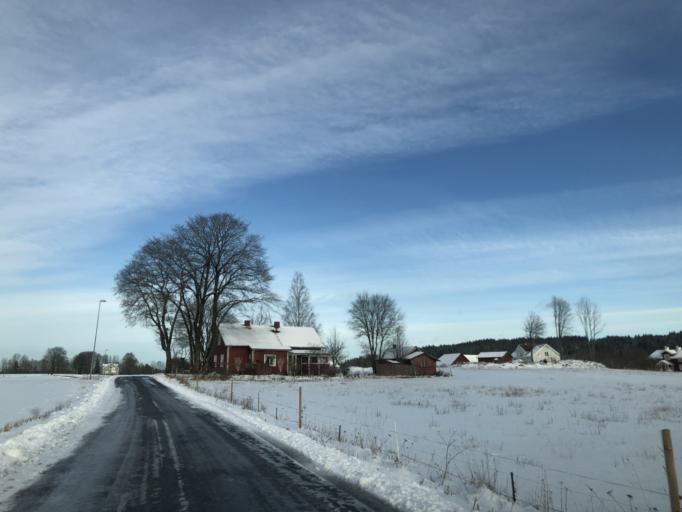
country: SE
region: Vaestra Goetaland
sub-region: Ulricehamns Kommun
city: Ulricehamn
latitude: 57.7833
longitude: 13.5254
